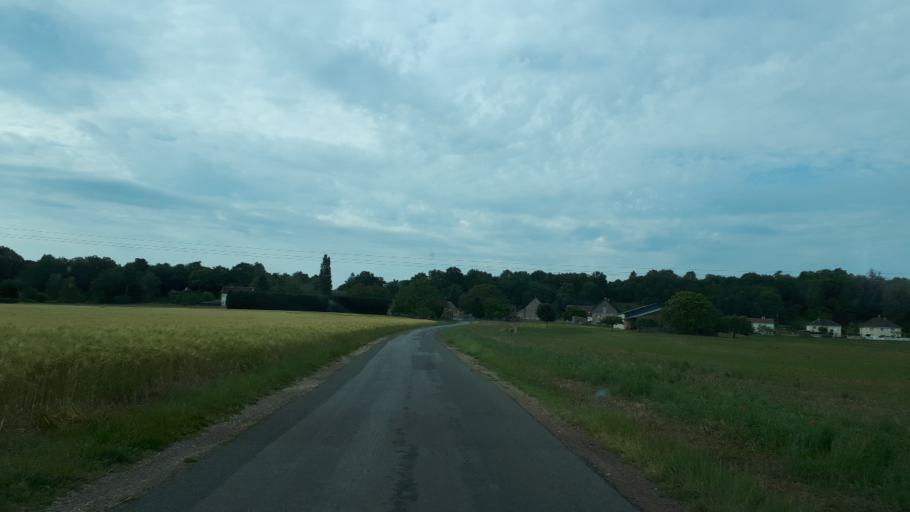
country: FR
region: Centre
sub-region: Departement du Loir-et-Cher
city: Villiers-sur-Loir
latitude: 47.7770
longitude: 1.0070
